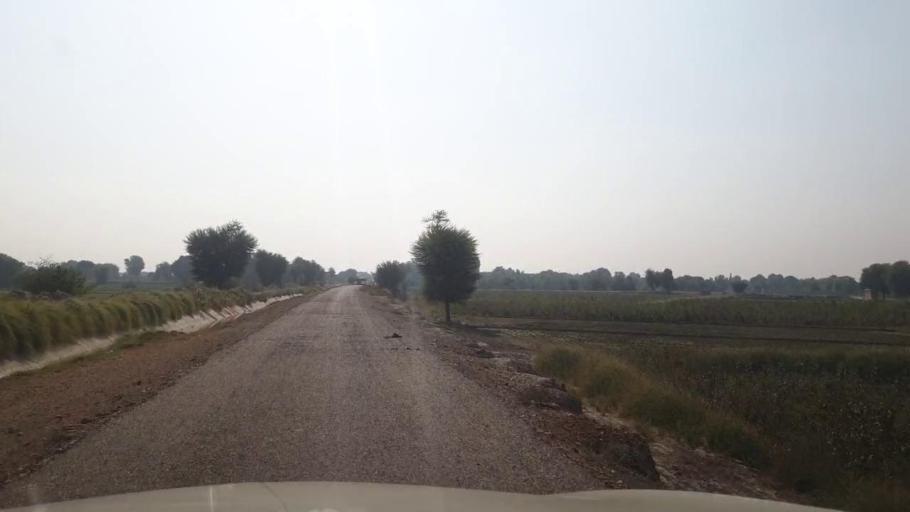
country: PK
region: Sindh
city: Bhan
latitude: 26.5203
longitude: 67.7799
